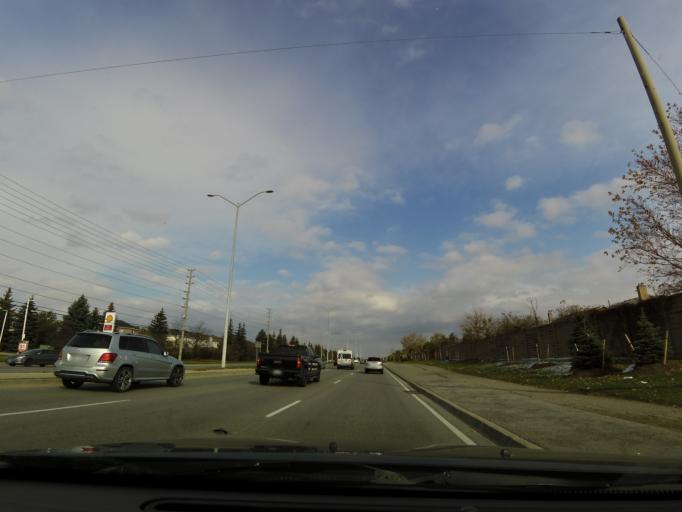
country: CA
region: Ontario
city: Brampton
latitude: 43.7309
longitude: -79.7587
